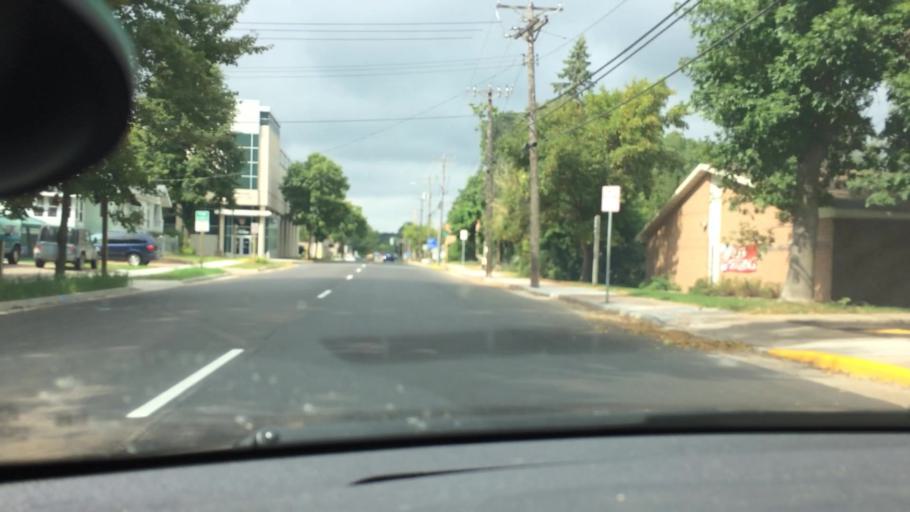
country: US
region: Wisconsin
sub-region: Chippewa County
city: Chippewa Falls
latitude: 44.9405
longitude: -91.3938
